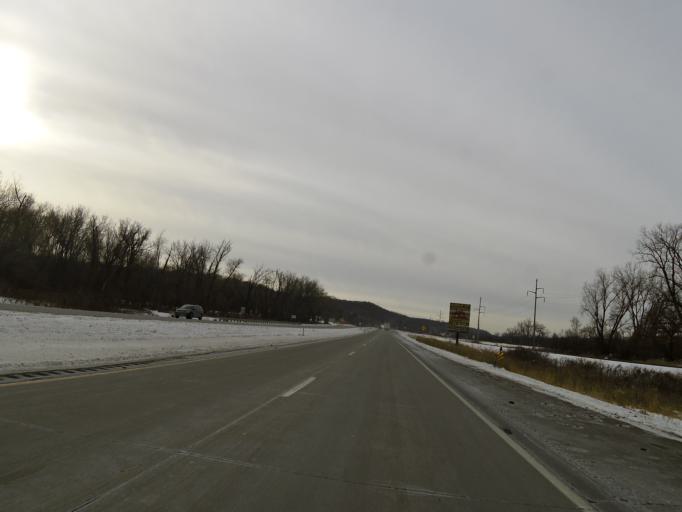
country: US
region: Minnesota
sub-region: Scott County
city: Jordan
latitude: 44.7031
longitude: -93.5955
